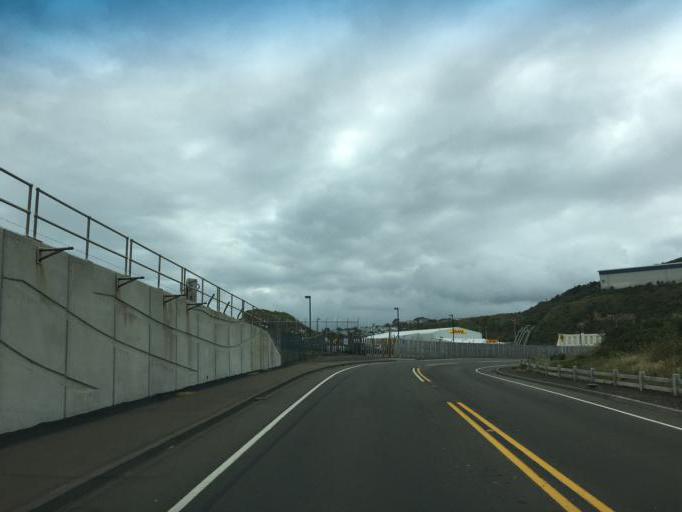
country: NZ
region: Wellington
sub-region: Wellington City
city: Wellington
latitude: -41.3360
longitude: 174.8075
